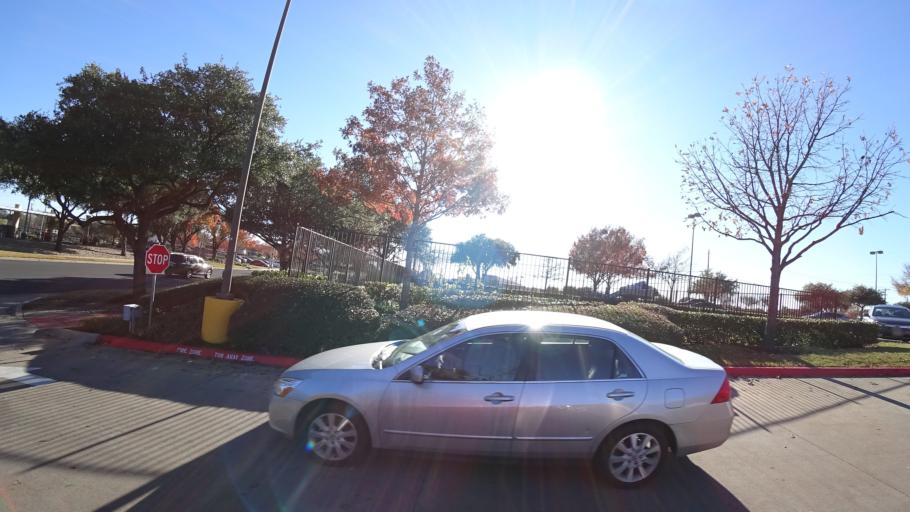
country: US
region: Texas
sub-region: Travis County
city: Wells Branch
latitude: 30.4121
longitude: -97.6865
